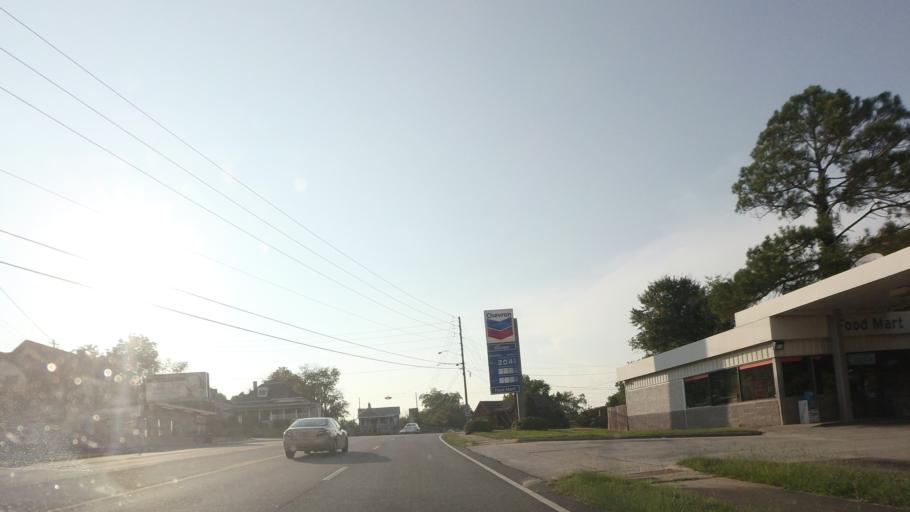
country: US
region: Georgia
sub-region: Bibb County
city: Macon
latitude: 32.8470
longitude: -83.6368
